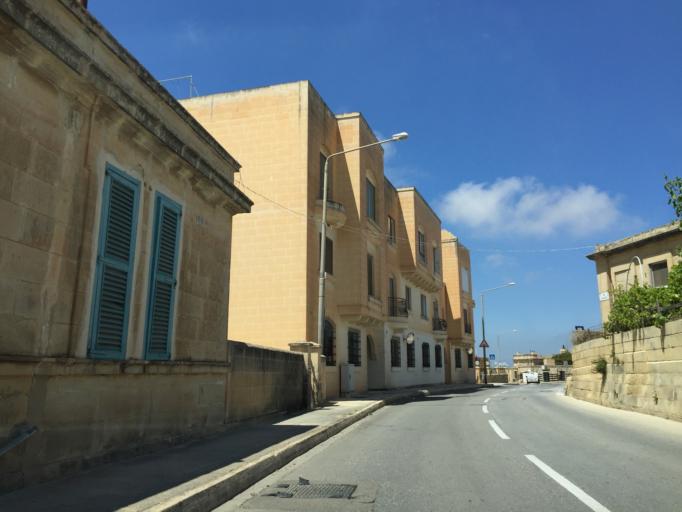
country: MT
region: L-Imtarfa
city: Imtarfa
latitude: 35.8929
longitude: 14.3981
